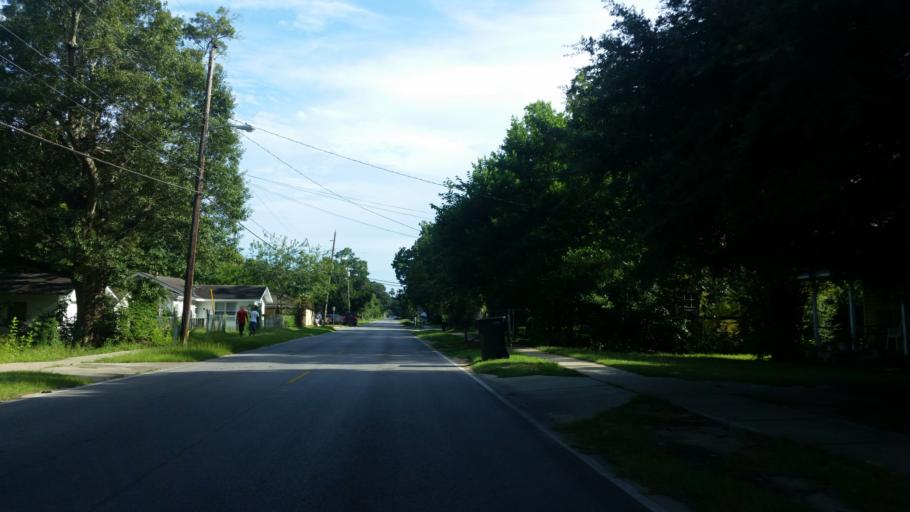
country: US
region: Florida
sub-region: Escambia County
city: Goulding
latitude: 30.4275
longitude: -87.2465
